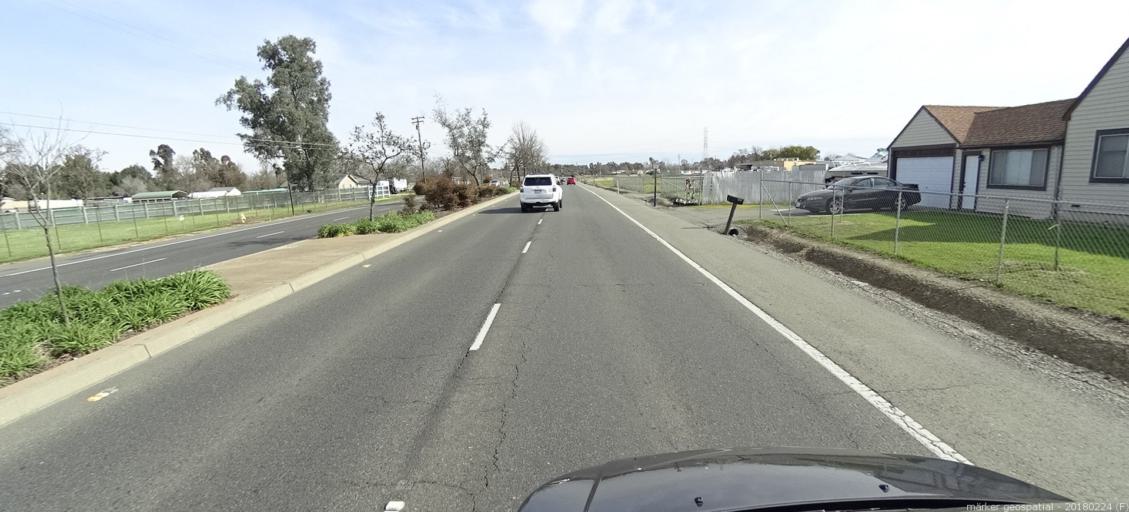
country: US
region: California
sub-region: Sacramento County
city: Rio Linda
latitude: 38.6862
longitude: -121.4323
